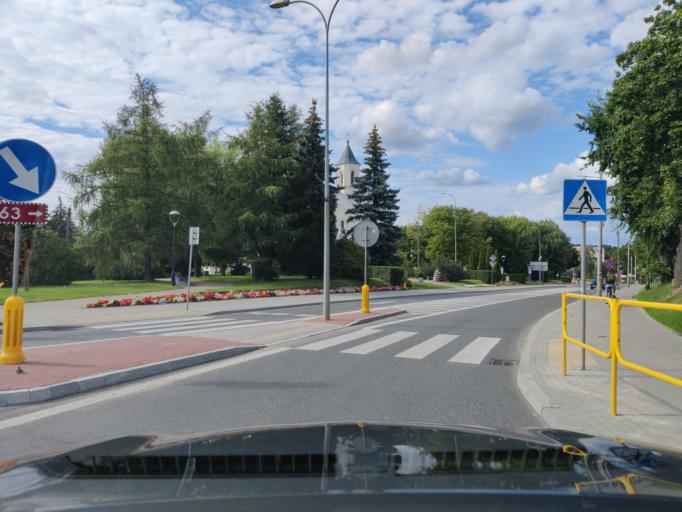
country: PL
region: Podlasie
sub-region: Powiat zambrowski
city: Zambrow
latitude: 52.9804
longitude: 22.2453
